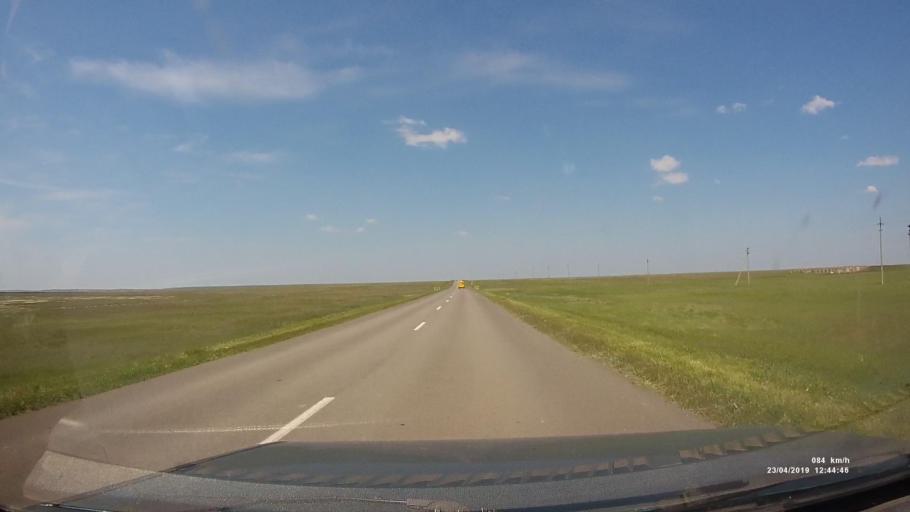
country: RU
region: Kalmykiya
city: Yashalta
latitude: 46.4809
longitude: 42.6456
